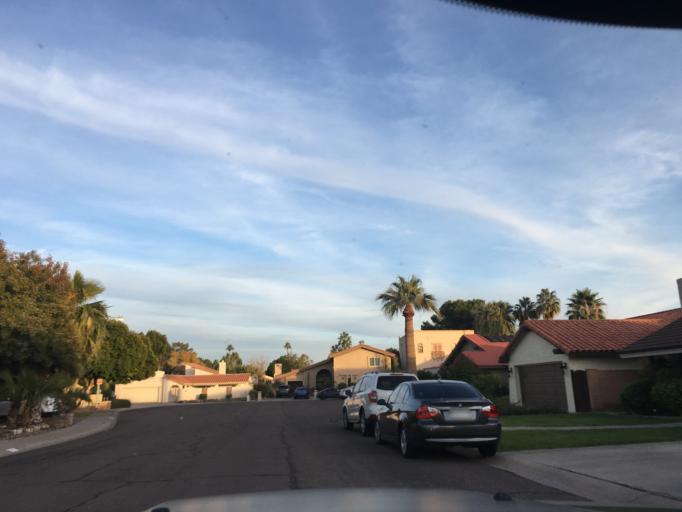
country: US
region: Arizona
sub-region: Maricopa County
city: Tempe
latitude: 33.3737
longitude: -111.9165
